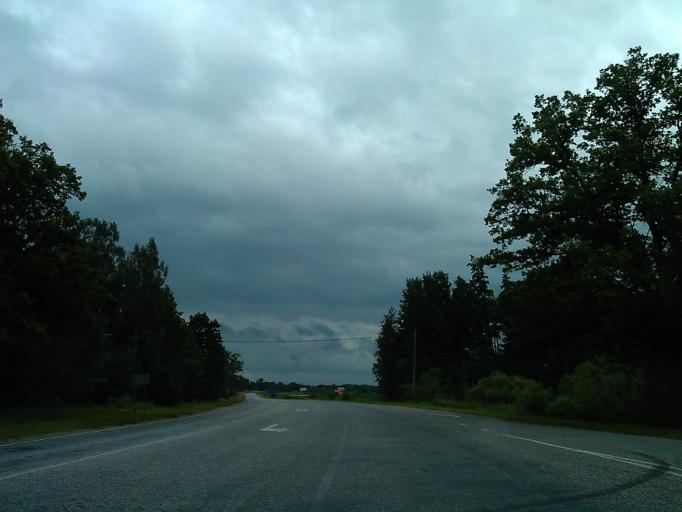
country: LV
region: Kuldigas Rajons
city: Kuldiga
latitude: 56.9795
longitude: 22.0167
